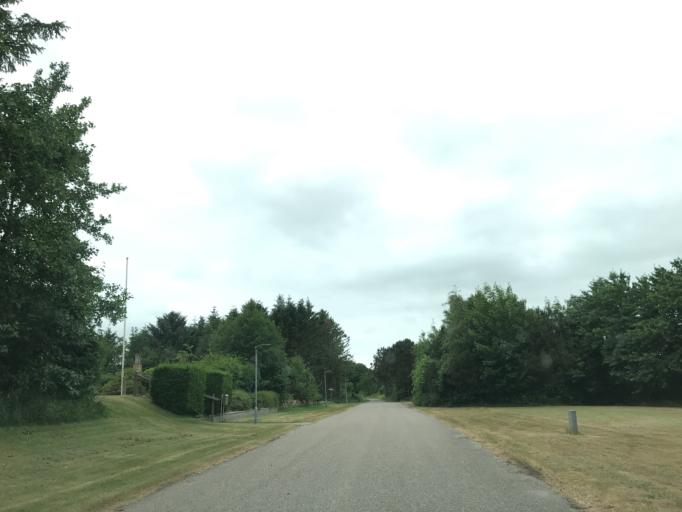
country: DK
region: South Denmark
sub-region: Tonder Kommune
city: Sherrebek
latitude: 55.0599
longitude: 8.8108
